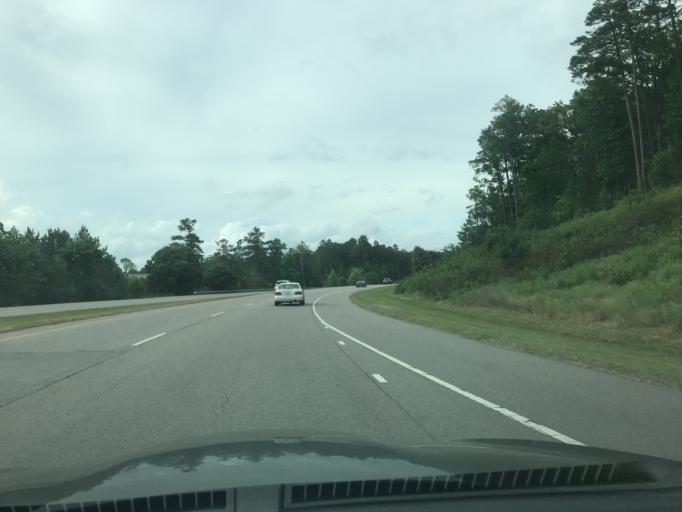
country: US
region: North Carolina
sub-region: Wake County
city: Morrisville
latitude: 35.8617
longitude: -78.8730
